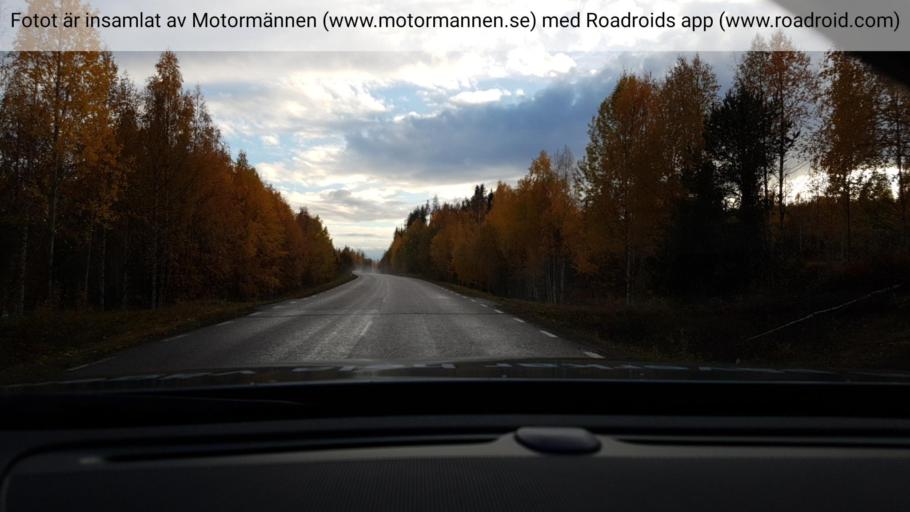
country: SE
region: Norrbotten
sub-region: Overkalix Kommun
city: OEverkalix
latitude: 66.7895
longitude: 22.7202
